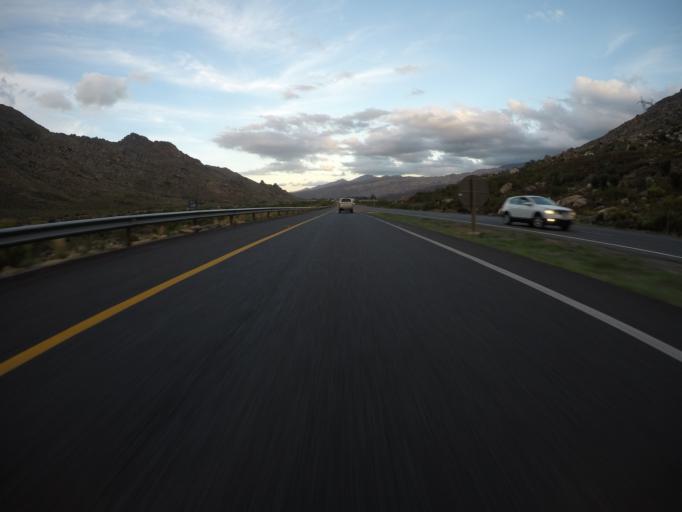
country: ZA
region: Western Cape
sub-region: Cape Winelands District Municipality
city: Worcester
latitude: -33.7013
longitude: 19.2269
